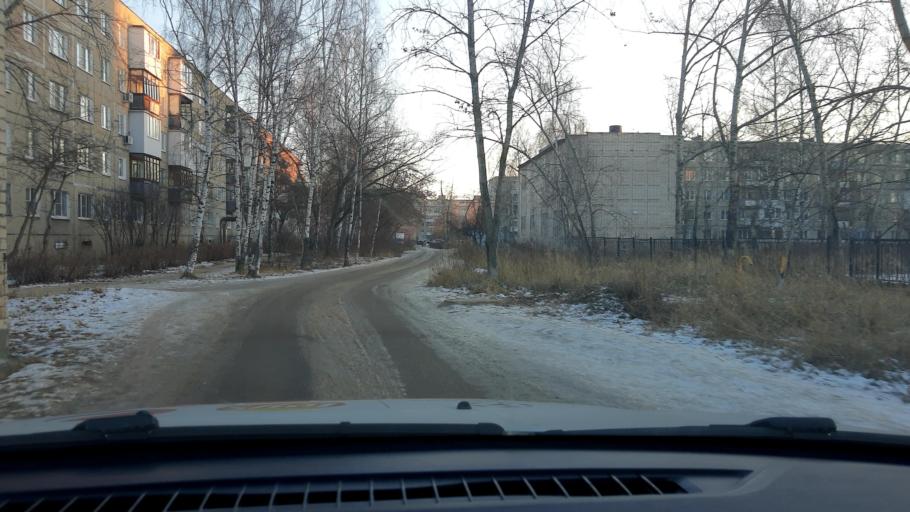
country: RU
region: Nizjnij Novgorod
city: Dzerzhinsk
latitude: 56.2333
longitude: 43.4002
